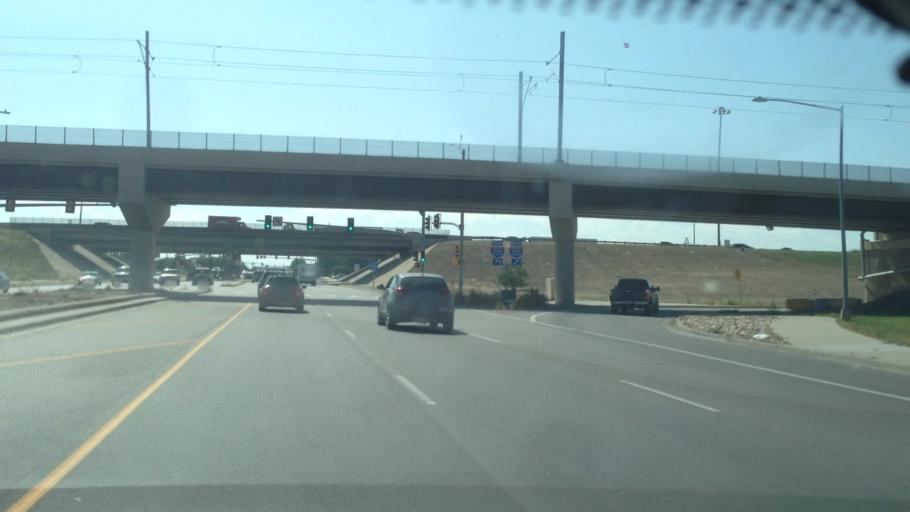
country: US
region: Colorado
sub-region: Adams County
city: Aurora
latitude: 39.7257
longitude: -104.8225
